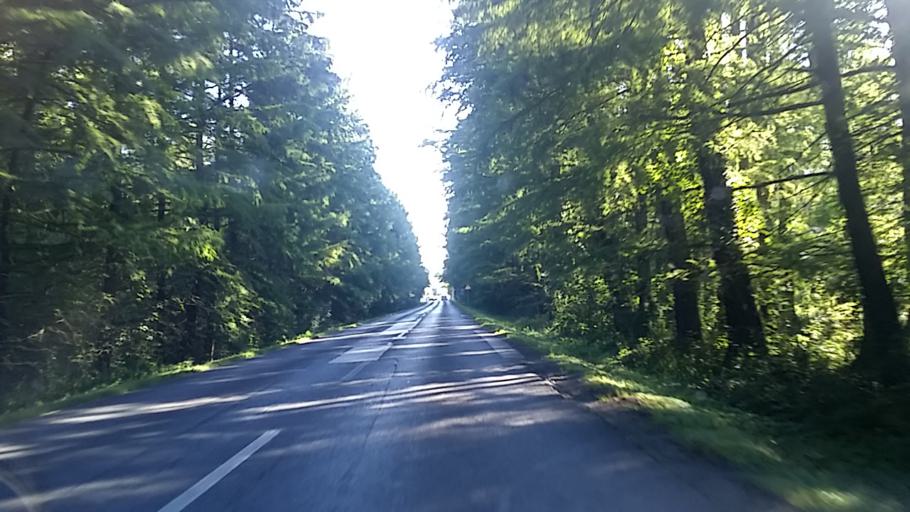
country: HU
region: Zala
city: Heviz
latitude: 46.7874
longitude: 17.1951
